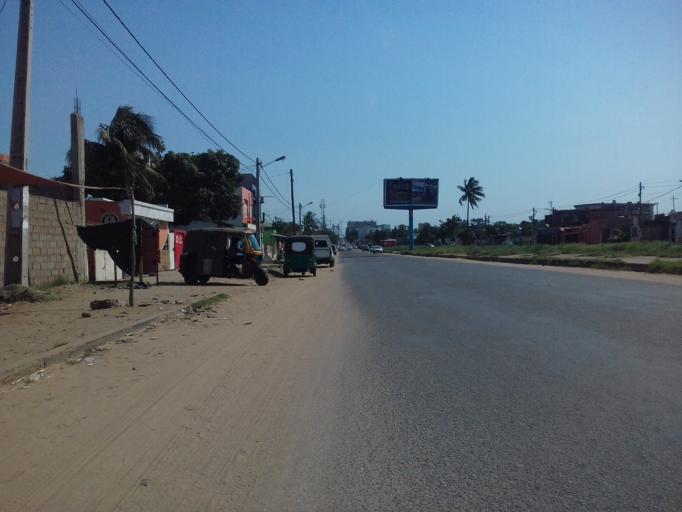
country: MZ
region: Maputo City
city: Maputo
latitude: -25.9469
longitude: 32.5714
